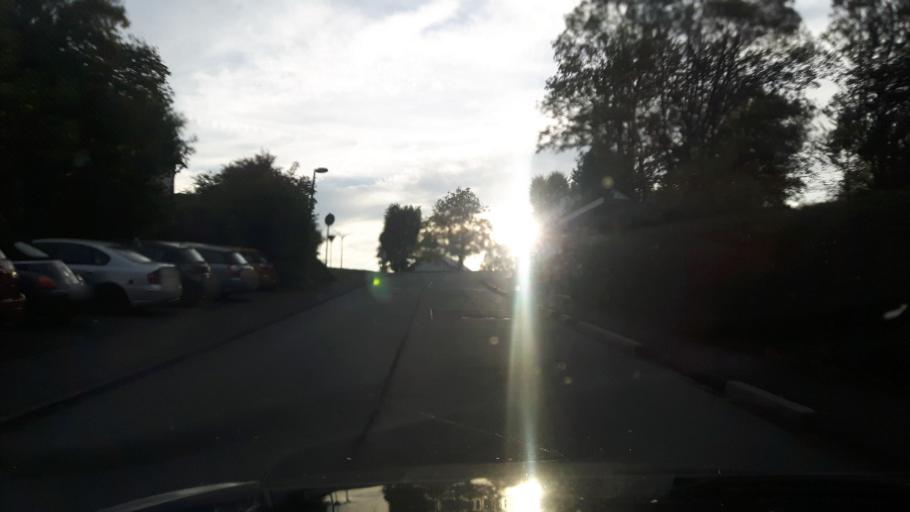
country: DE
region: North Rhine-Westphalia
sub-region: Regierungsbezirk Arnsberg
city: Bad Laasphe
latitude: 50.9257
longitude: 8.4046
